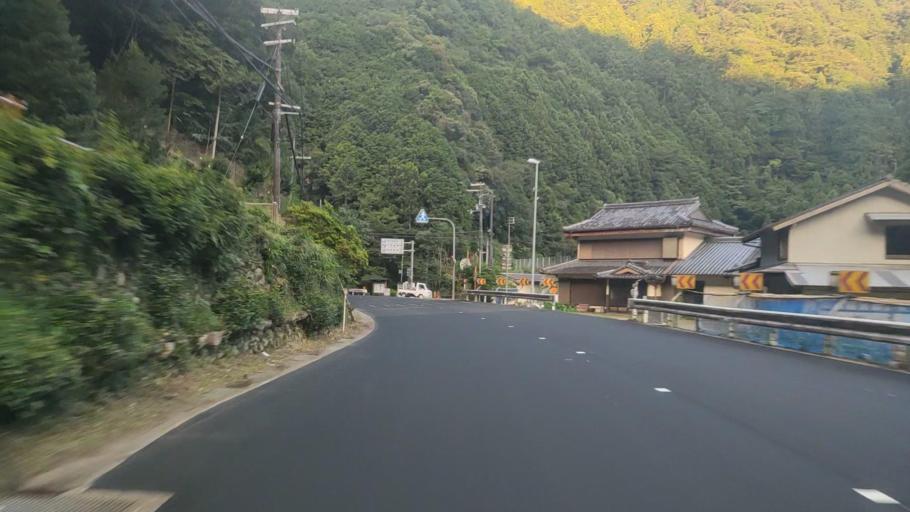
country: JP
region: Wakayama
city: Shingu
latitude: 33.8067
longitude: 135.7125
